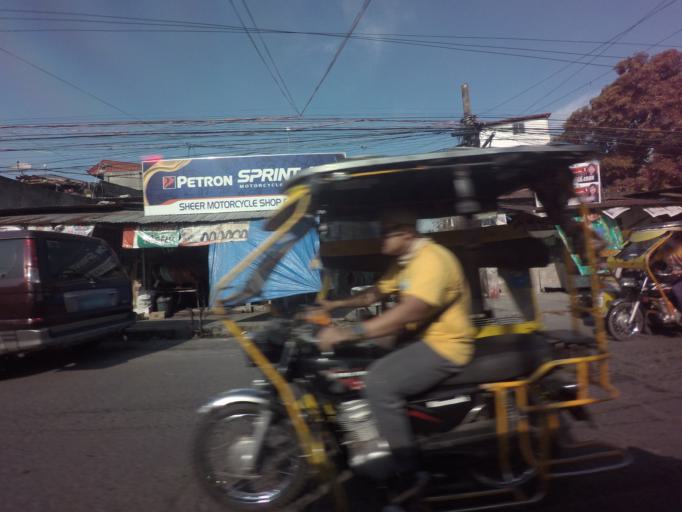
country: PH
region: Calabarzon
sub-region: Province of Rizal
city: Taguig
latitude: 14.4999
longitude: 121.0517
